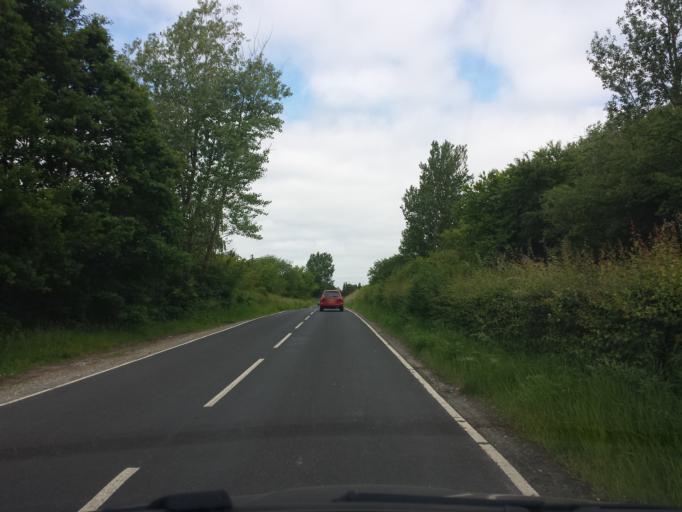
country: DK
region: Capital Region
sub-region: Glostrup Kommune
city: Glostrup
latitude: 55.7072
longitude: 12.3979
